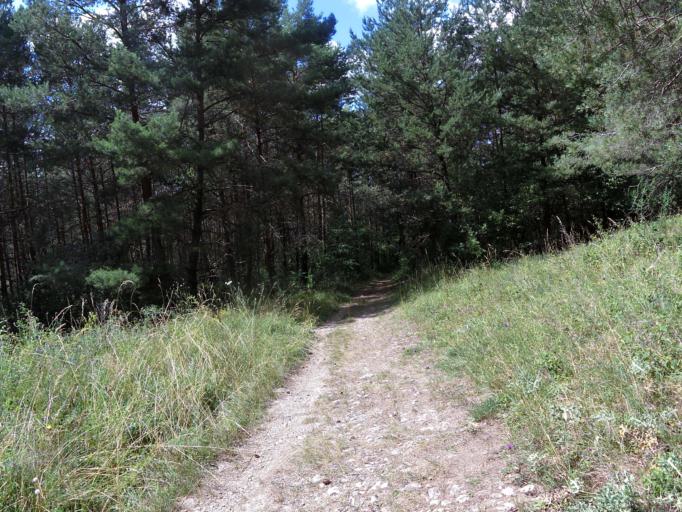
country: DE
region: Bavaria
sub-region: Regierungsbezirk Unterfranken
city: Gerbrunn
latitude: 49.7714
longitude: 9.9984
